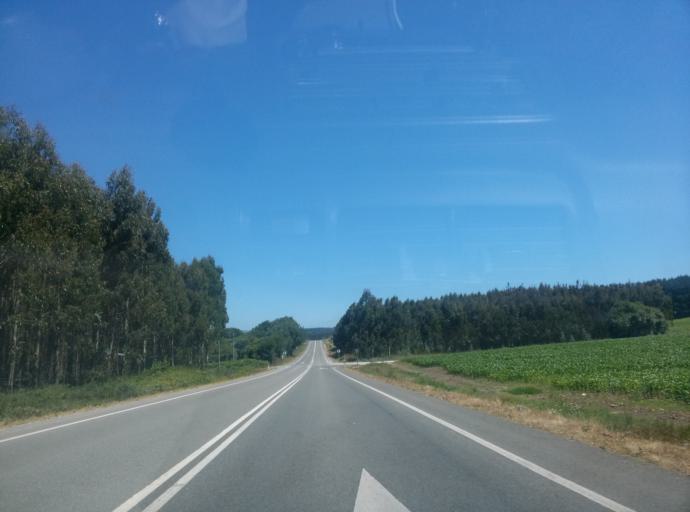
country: ES
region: Galicia
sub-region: Provincia de Lugo
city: Castro de Rei
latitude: 43.2370
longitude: -7.4053
